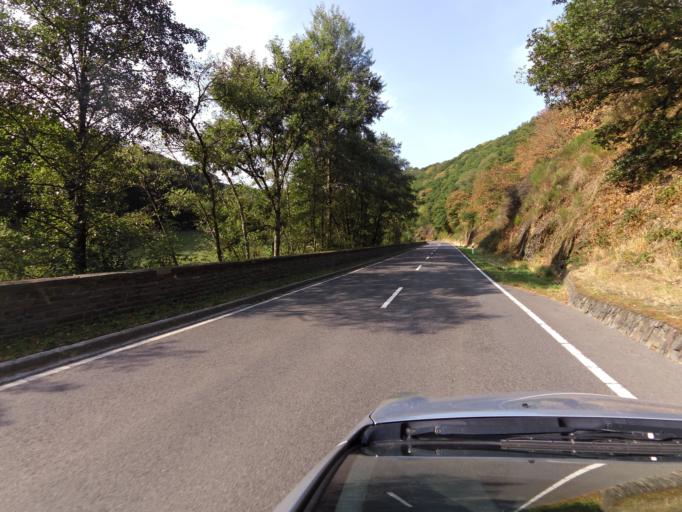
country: LU
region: Diekirch
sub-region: Canton de Diekirch
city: Bourscheid
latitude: 49.9268
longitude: 6.0677
